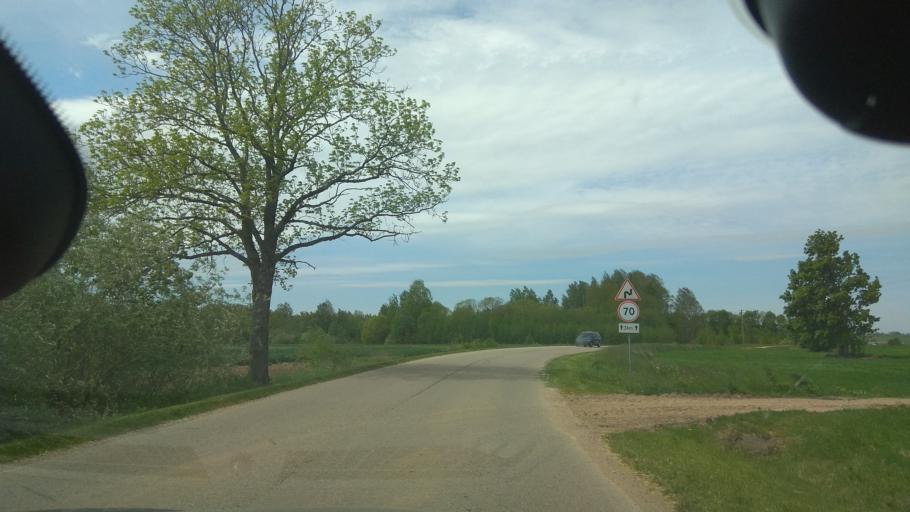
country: LT
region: Vilnius County
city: Ukmerge
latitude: 55.1486
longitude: 24.5608
